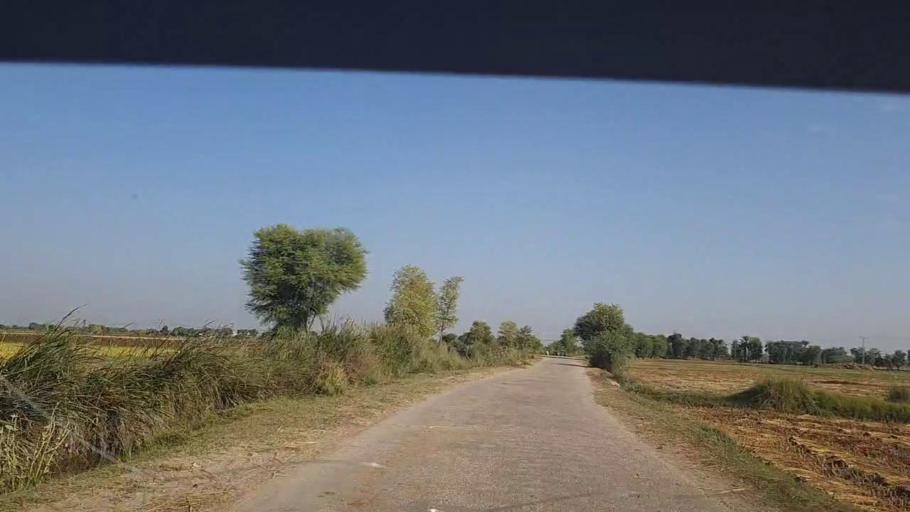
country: PK
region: Sindh
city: Larkana
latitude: 27.6233
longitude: 68.2413
